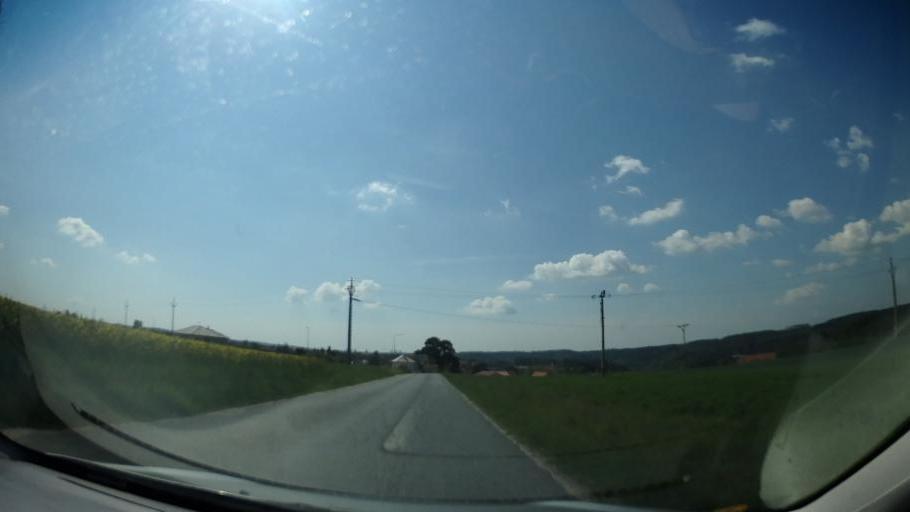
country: CZ
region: Vysocina
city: Hrotovice
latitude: 49.1758
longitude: 16.0843
